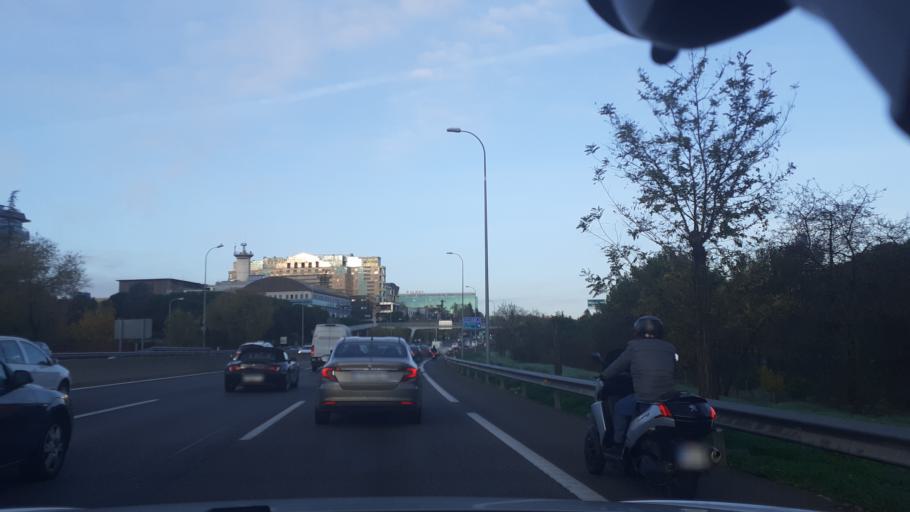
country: ES
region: Madrid
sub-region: Provincia de Madrid
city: Ciudad Lineal
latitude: 40.4487
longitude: -3.6364
